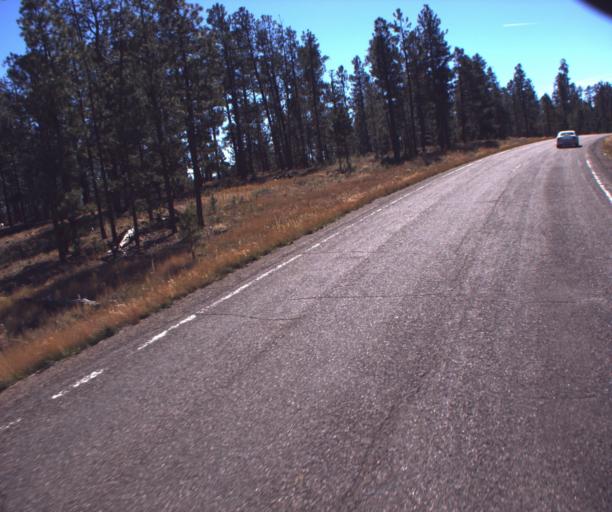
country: US
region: Arizona
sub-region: Coconino County
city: Fredonia
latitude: 36.7325
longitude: -112.2123
